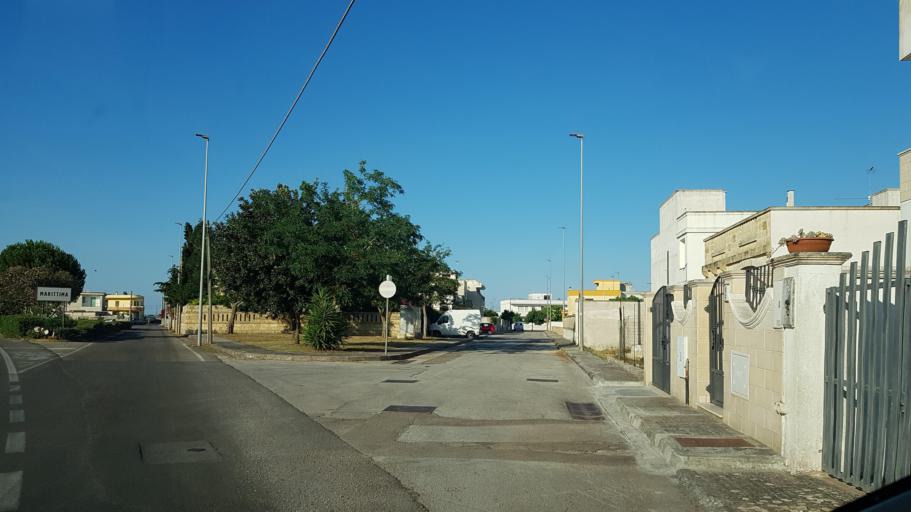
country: IT
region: Apulia
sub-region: Provincia di Lecce
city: Marittima
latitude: 39.9980
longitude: 18.3933
